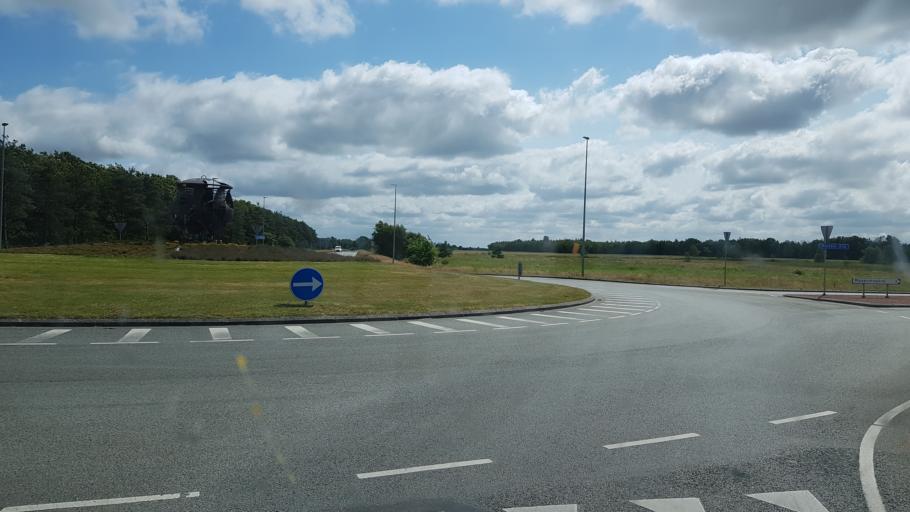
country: DK
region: South Denmark
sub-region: Billund Kommune
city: Grindsted
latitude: 55.7548
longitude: 8.9027
